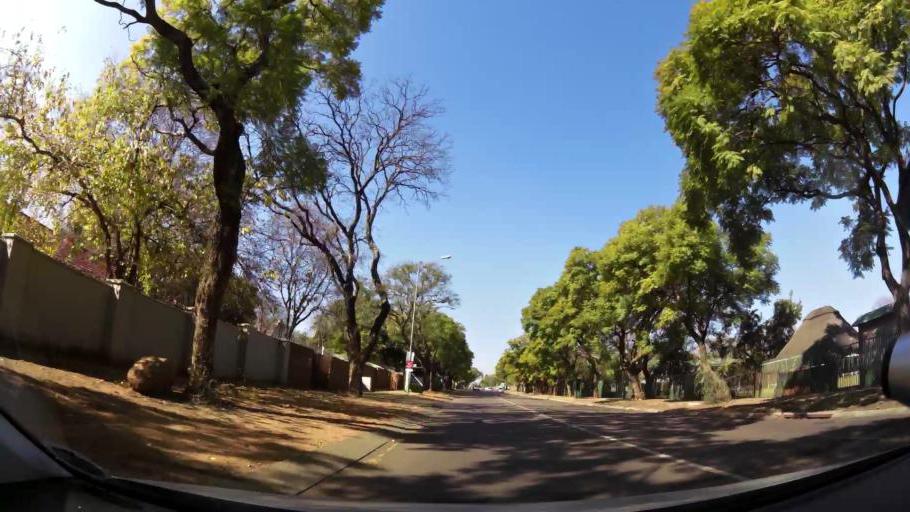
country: ZA
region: Gauteng
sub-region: City of Tshwane Metropolitan Municipality
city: Pretoria
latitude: -25.7656
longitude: 28.2307
